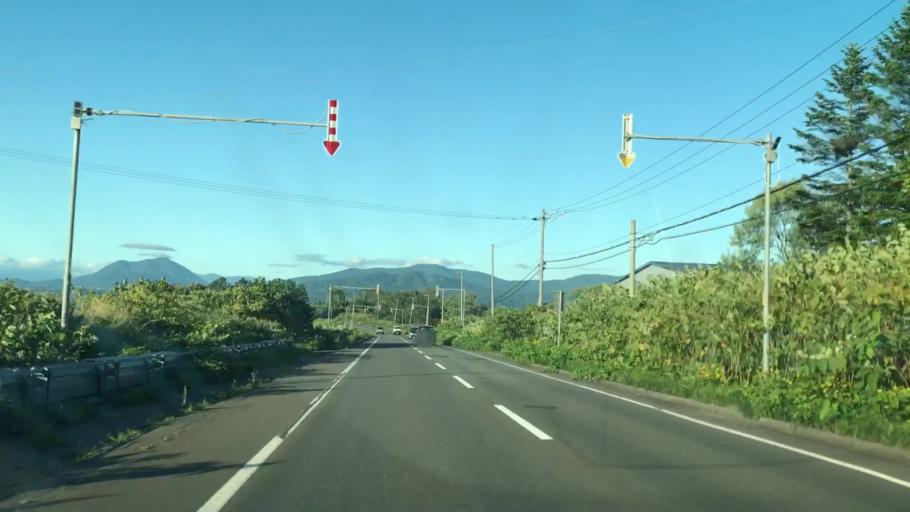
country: JP
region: Hokkaido
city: Date
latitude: 42.6168
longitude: 140.7894
